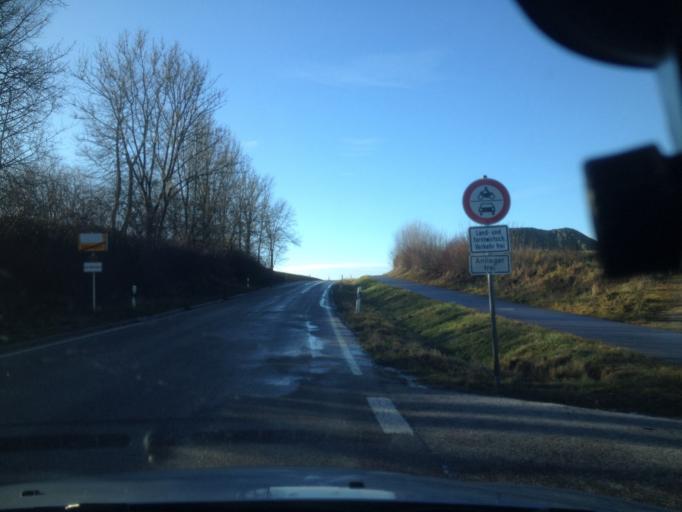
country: DE
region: Bavaria
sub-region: Swabia
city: Offingen
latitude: 48.4742
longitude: 10.3601
